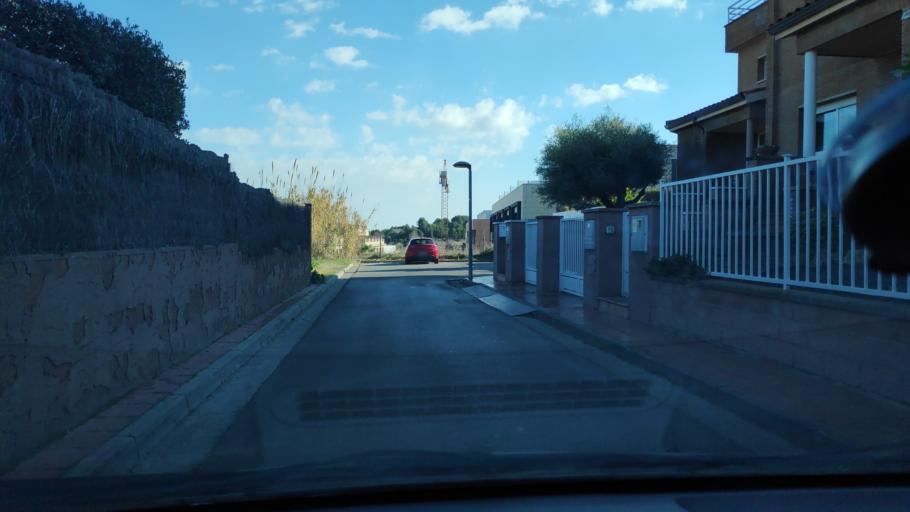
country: ES
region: Catalonia
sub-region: Provincia de Barcelona
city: Sant Quirze del Valles
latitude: 41.5245
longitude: 2.0731
